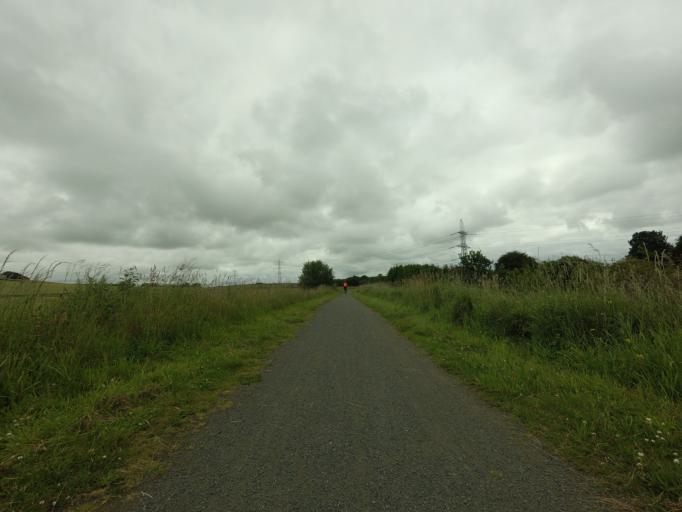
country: GB
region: Scotland
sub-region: Aberdeenshire
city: Mintlaw
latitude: 57.4942
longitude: -2.1374
